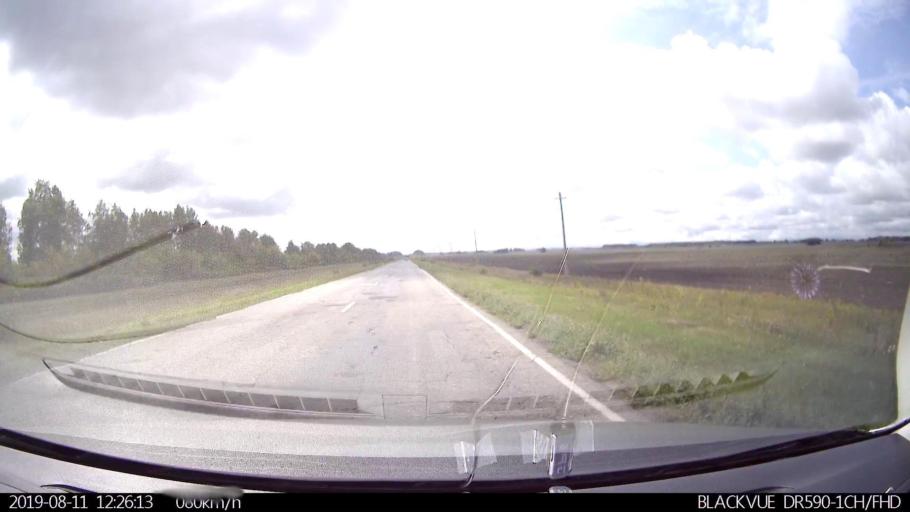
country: RU
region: Ulyanovsk
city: Ignatovka
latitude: 53.8661
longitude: 47.9321
